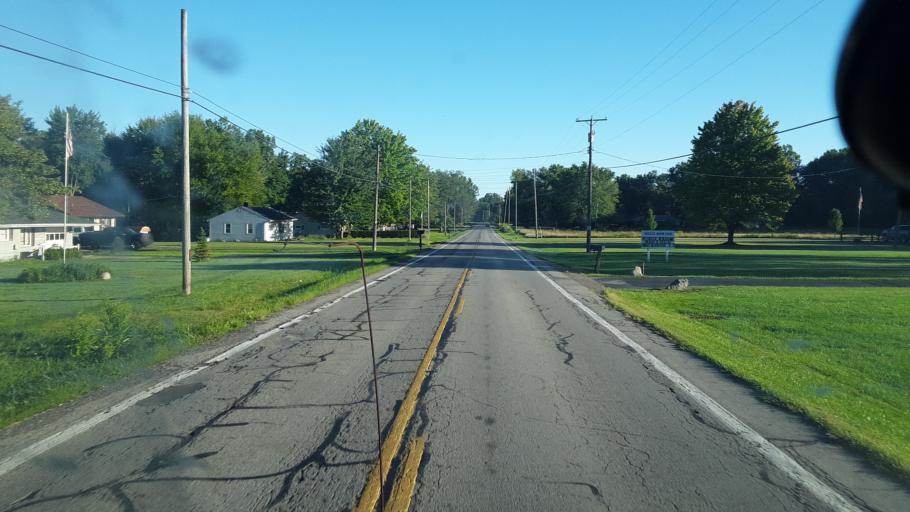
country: US
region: Ohio
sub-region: Trumbull County
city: Newton Falls
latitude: 41.2393
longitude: -80.9757
